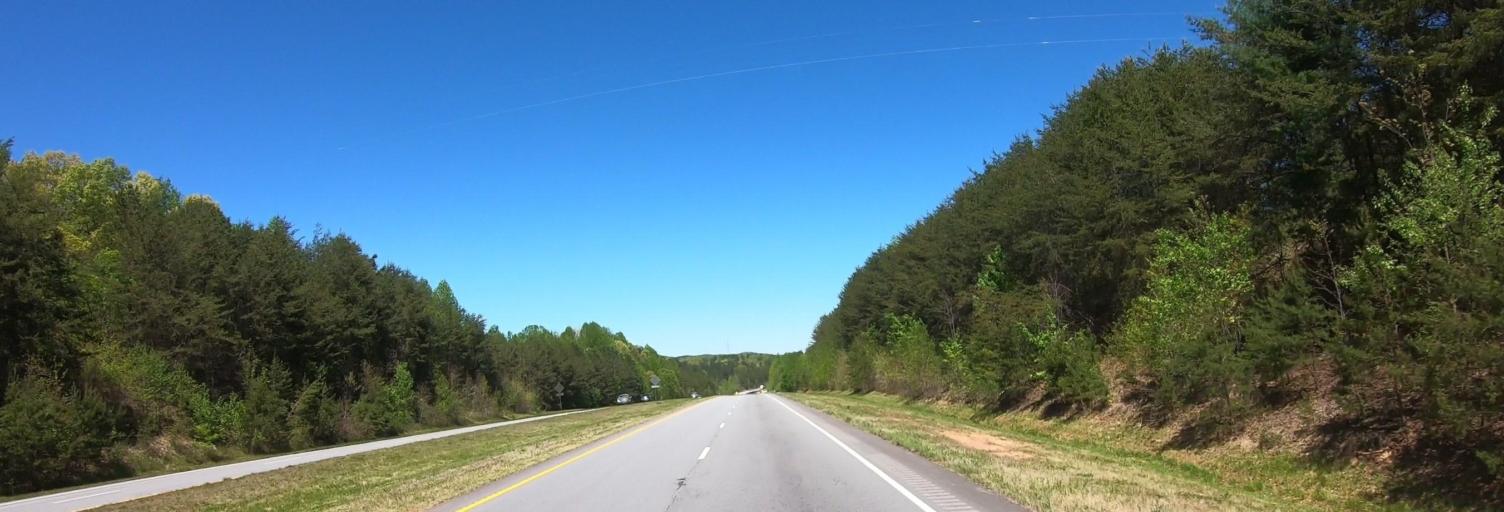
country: US
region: Georgia
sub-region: Habersham County
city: Clarkesville
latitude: 34.6912
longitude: -83.4242
